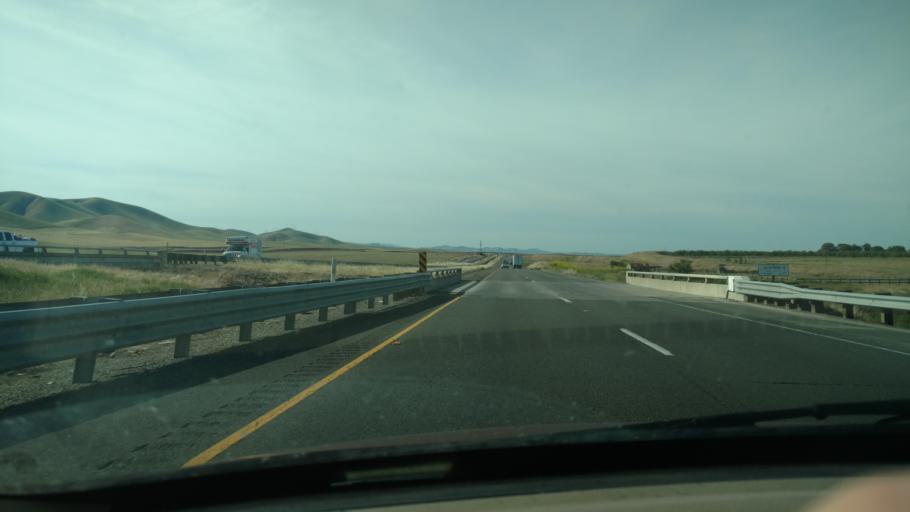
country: US
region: California
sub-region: Merced County
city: Gustine
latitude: 37.1772
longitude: -121.0630
